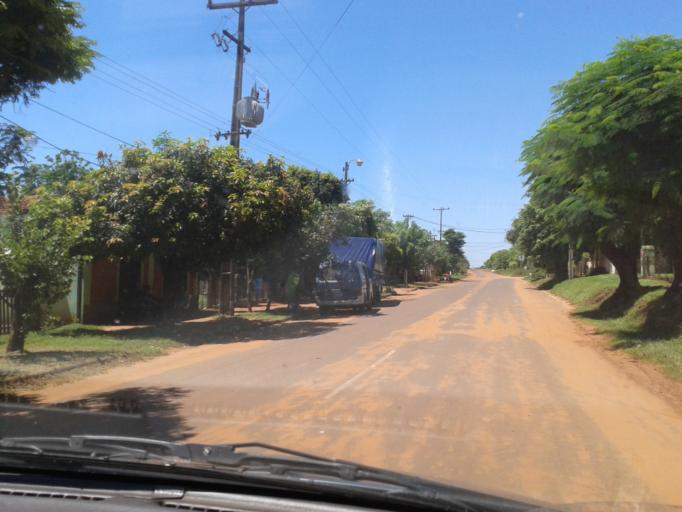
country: PY
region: Misiones
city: Santa Maria
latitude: -26.8975
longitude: -57.0277
